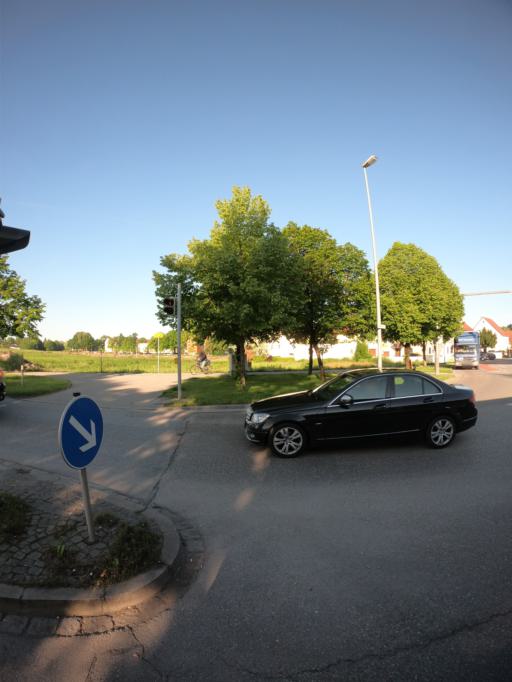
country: DE
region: Bavaria
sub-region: Upper Bavaria
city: Erding
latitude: 48.3046
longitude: 11.9187
